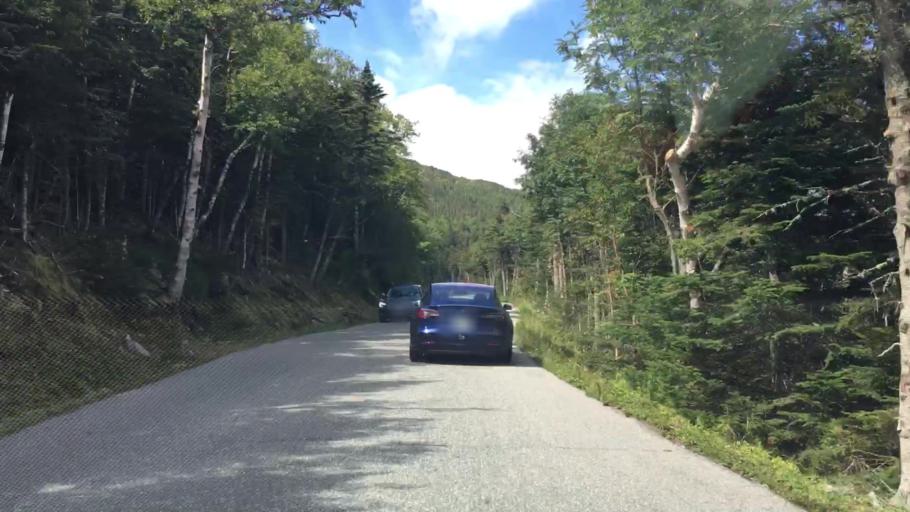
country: US
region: New Hampshire
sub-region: Coos County
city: Gorham
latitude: 44.2891
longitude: -71.2696
